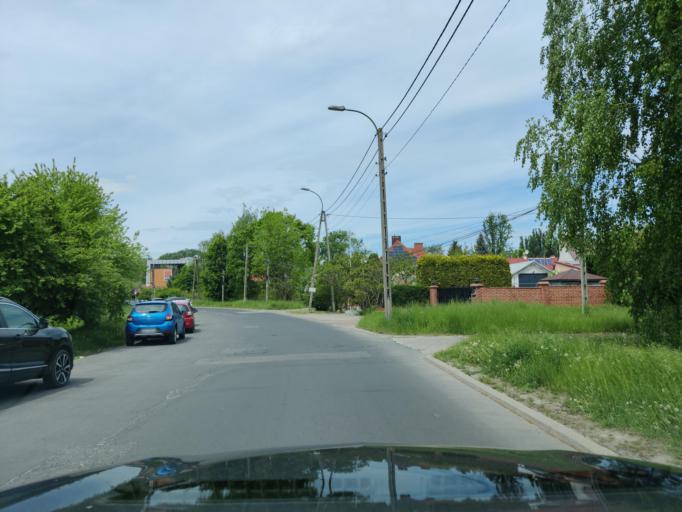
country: PL
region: Masovian Voivodeship
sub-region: Warszawa
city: Ursynow
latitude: 52.1562
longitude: 21.0045
